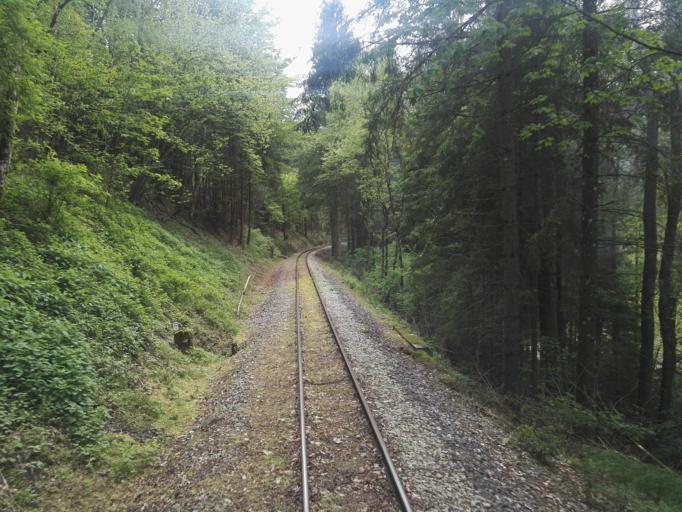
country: AT
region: Styria
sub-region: Politischer Bezirk Weiz
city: Birkfeld
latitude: 47.3377
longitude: 15.6996
